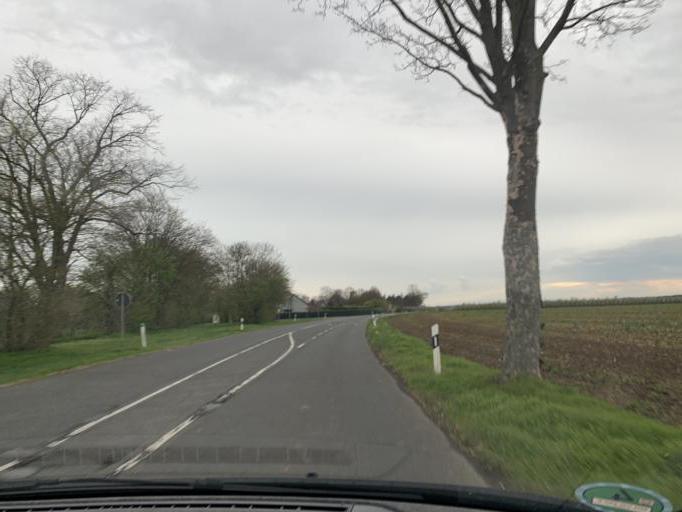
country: DE
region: North Rhine-Westphalia
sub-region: Regierungsbezirk Koln
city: Norvenich
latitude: 50.8013
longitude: 6.6997
